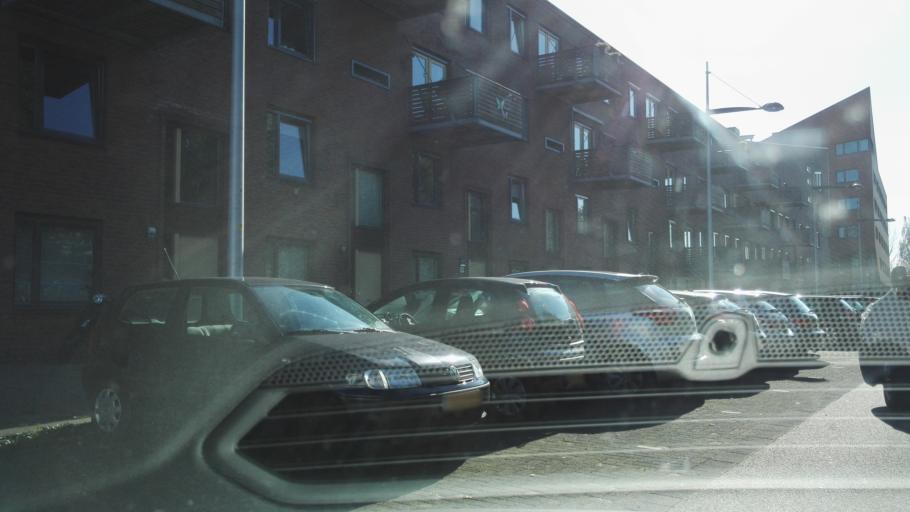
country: NL
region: Gelderland
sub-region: Gemeente Apeldoorn
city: Apeldoorn
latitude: 52.2164
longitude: 6.0027
